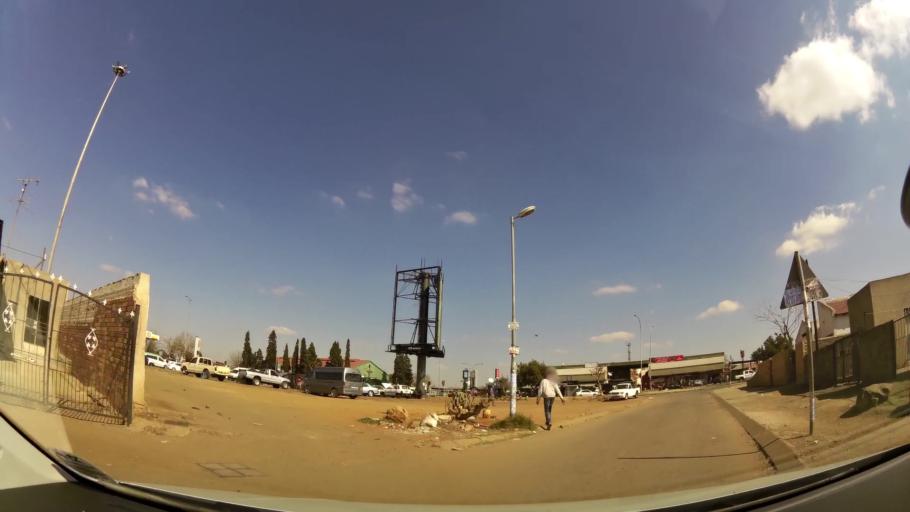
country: ZA
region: Gauteng
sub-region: City of Johannesburg Metropolitan Municipality
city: Soweto
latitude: -26.2507
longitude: 27.8851
